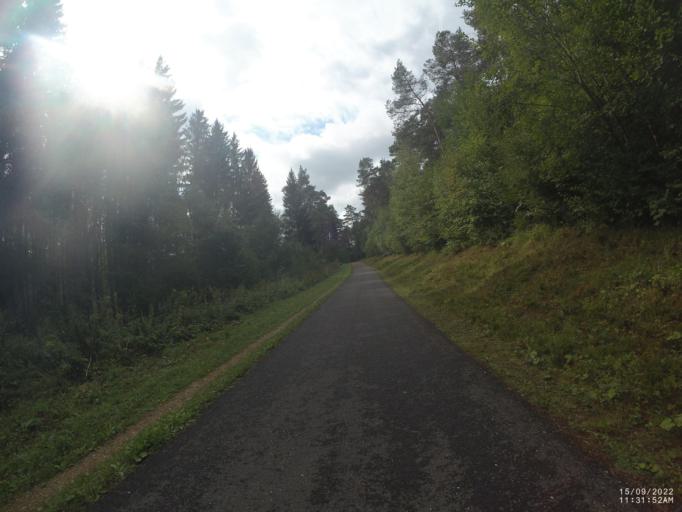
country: DE
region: Rheinland-Pfalz
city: Nohn
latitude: 50.3195
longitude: 6.7750
